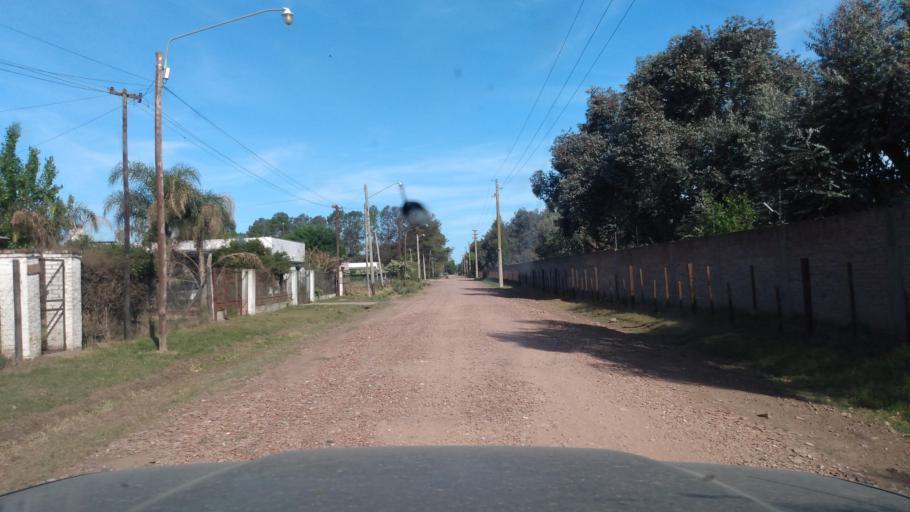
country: AR
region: Buenos Aires
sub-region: Partido de Lujan
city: Lujan
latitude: -34.5933
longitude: -59.1452
